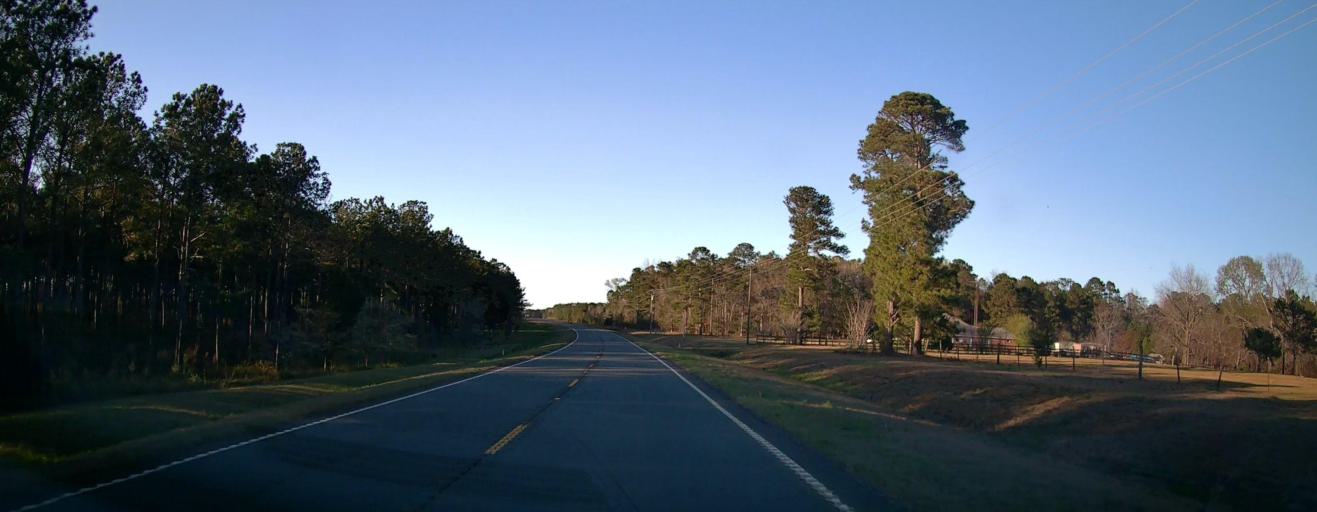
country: US
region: Georgia
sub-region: Talbot County
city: Talbotton
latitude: 32.6370
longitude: -84.5371
